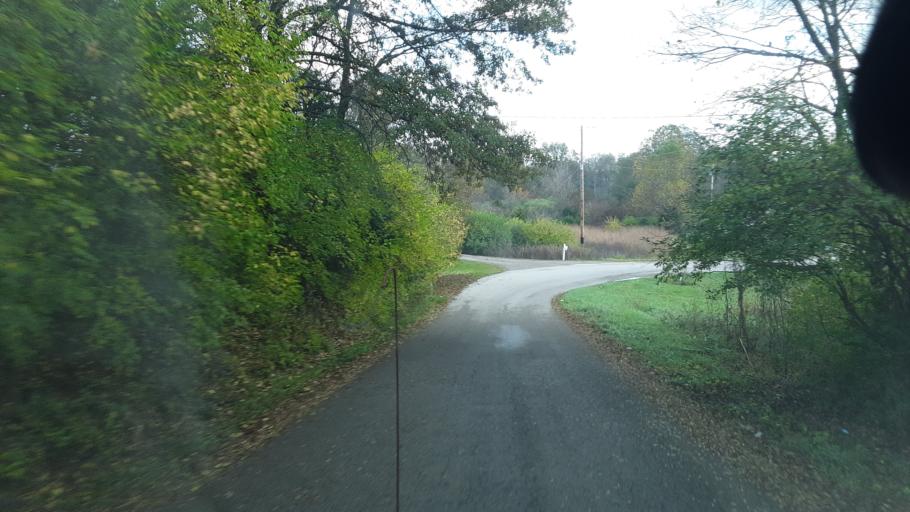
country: US
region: Ohio
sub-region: Highland County
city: Leesburg
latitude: 39.3352
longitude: -83.4712
